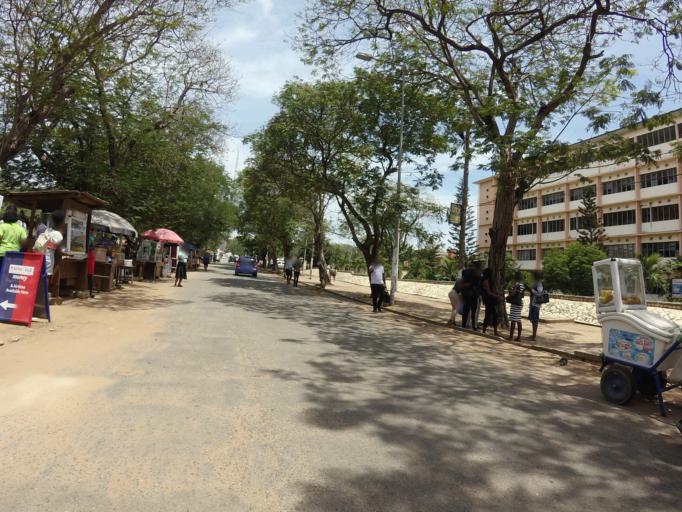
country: GH
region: Greater Accra
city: Accra
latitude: 5.5577
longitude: -0.2079
